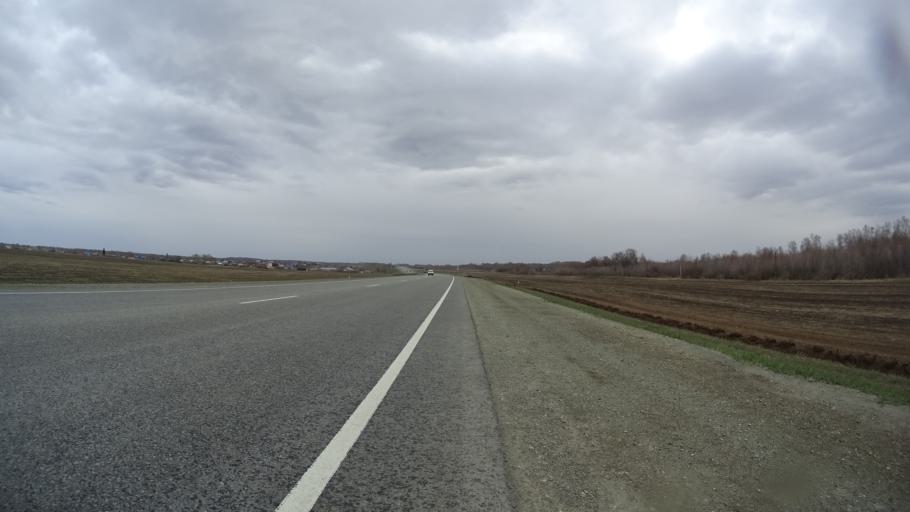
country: RU
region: Chelyabinsk
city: Krasnogorskiy
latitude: 54.6801
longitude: 61.2470
